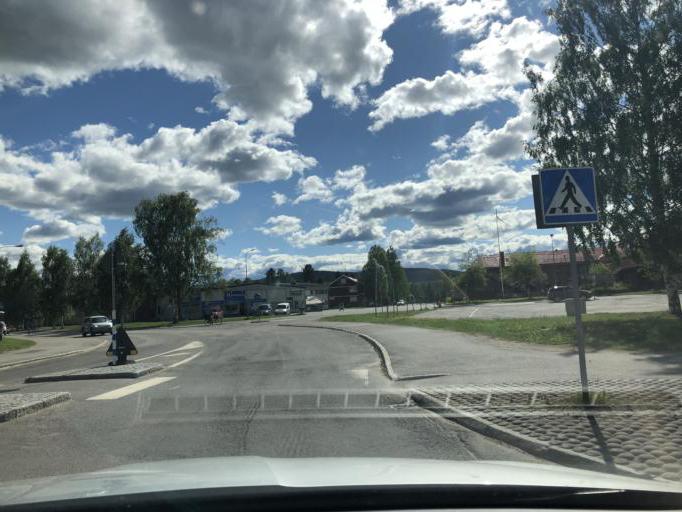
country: SE
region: Norrbotten
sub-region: Alvsbyns Kommun
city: AElvsbyn
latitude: 65.6748
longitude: 21.0058
